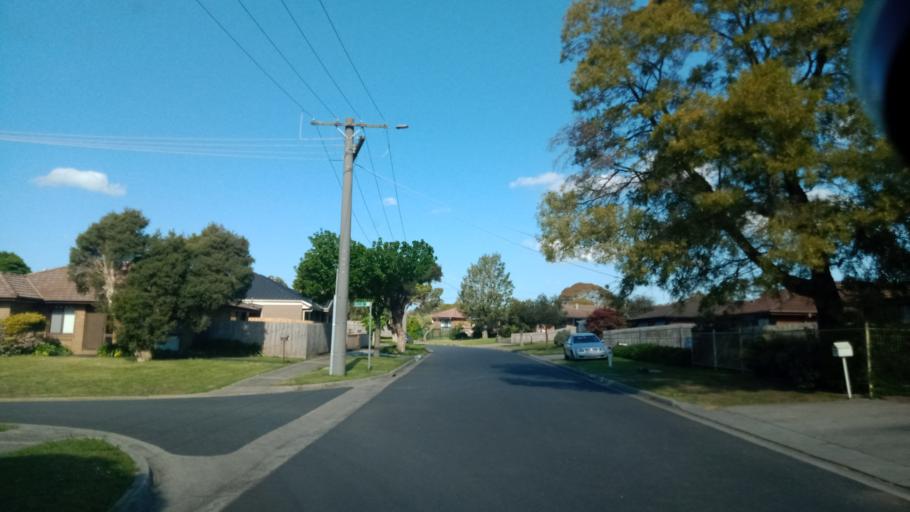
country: AU
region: Victoria
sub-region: Casey
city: Cranbourne West
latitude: -38.0998
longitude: 145.2695
